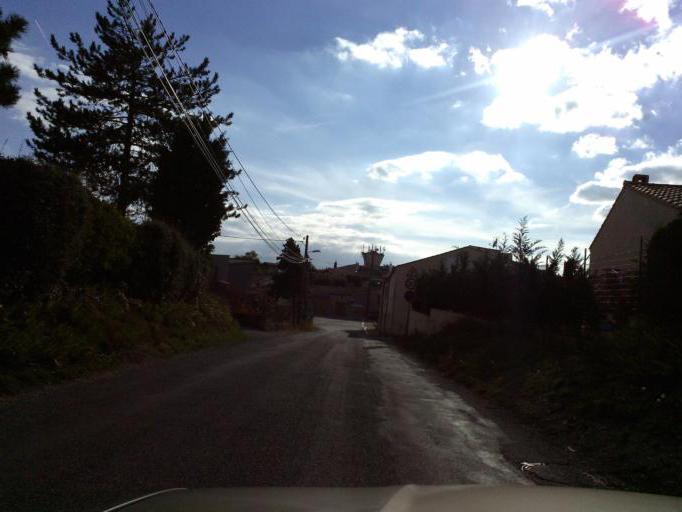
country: FR
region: Provence-Alpes-Cote d'Azur
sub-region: Departement des Alpes-de-Haute-Provence
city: Valensole
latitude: 43.8409
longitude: 5.9837
